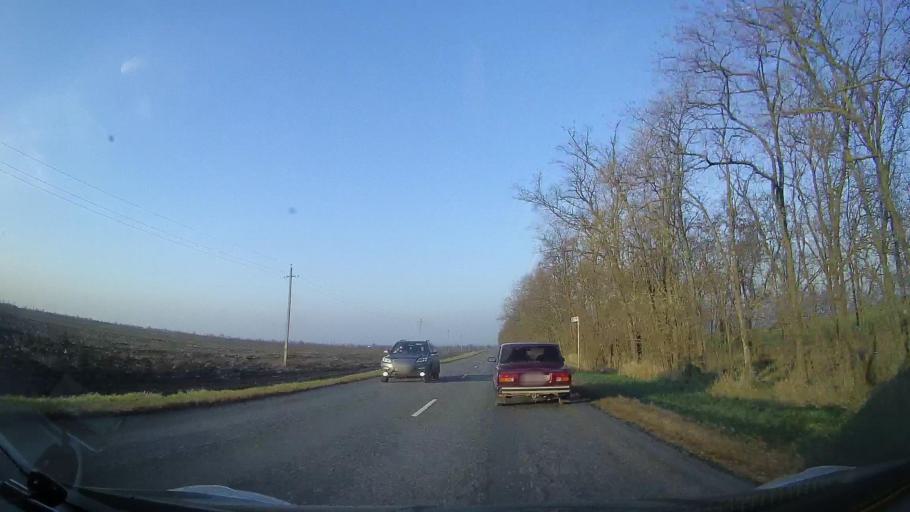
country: RU
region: Rostov
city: Ol'ginskaya
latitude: 47.0899
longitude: 39.9776
